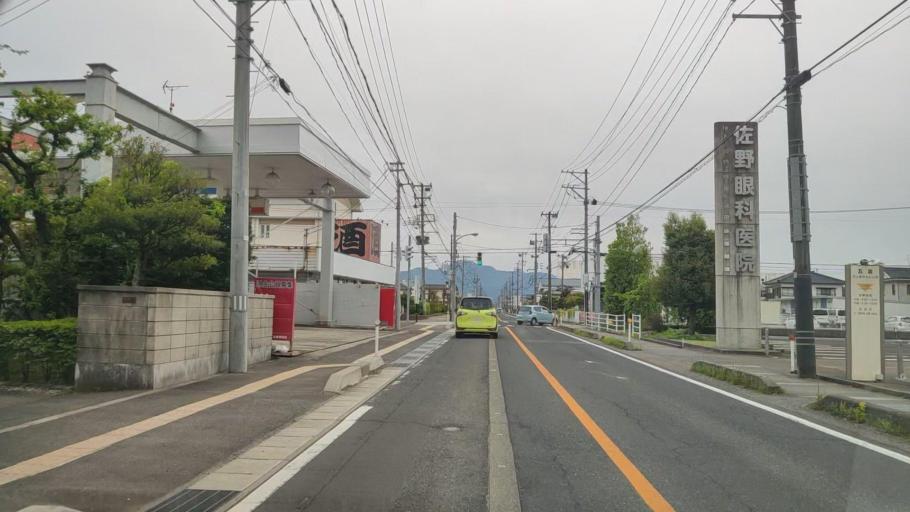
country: JP
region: Niigata
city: Gosen
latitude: 37.7339
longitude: 139.1767
